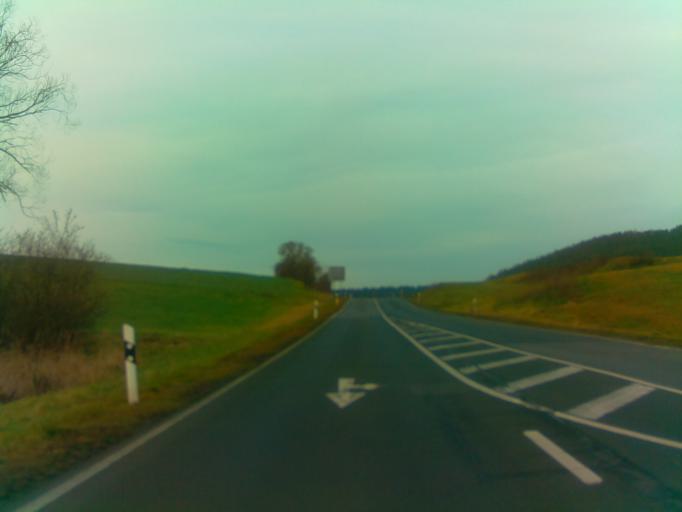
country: DE
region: Thuringia
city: Laasdorf
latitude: 50.8734
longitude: 11.6691
